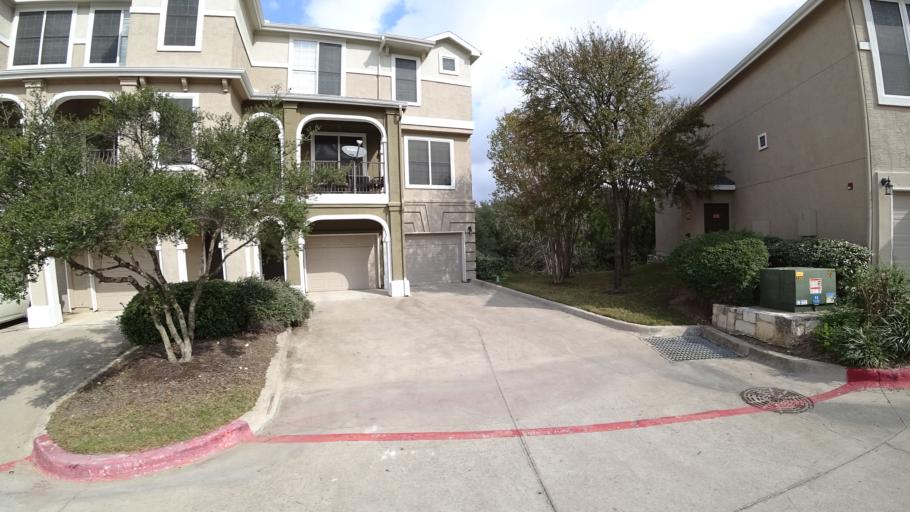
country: US
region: Texas
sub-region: Travis County
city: Hudson Bend
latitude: 30.3839
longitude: -97.8786
